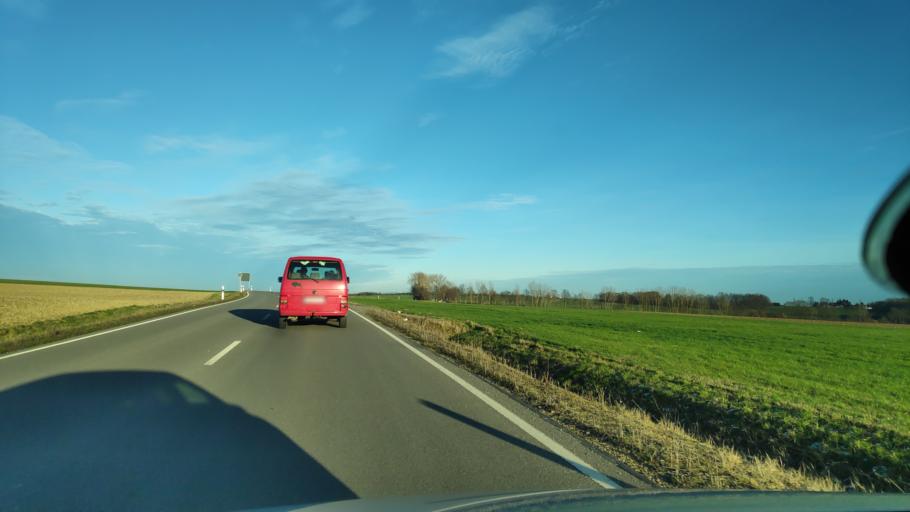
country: DE
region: Thuringia
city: Seelingstadt
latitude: 50.7961
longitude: 12.2452
